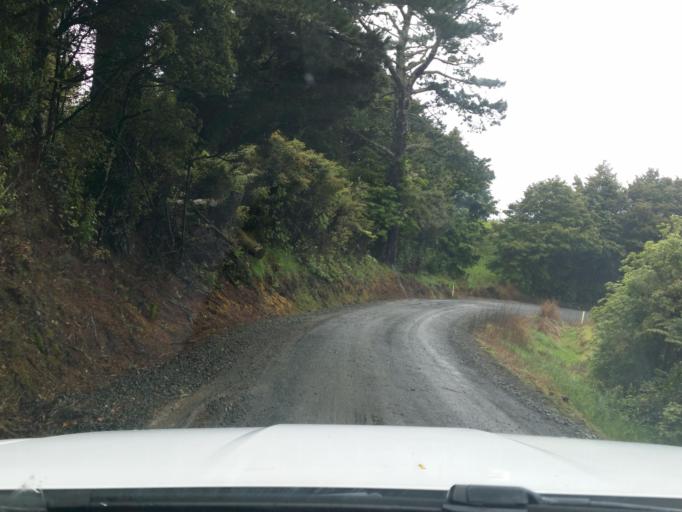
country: NZ
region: Northland
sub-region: Kaipara District
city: Dargaville
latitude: -35.7782
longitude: 173.9878
